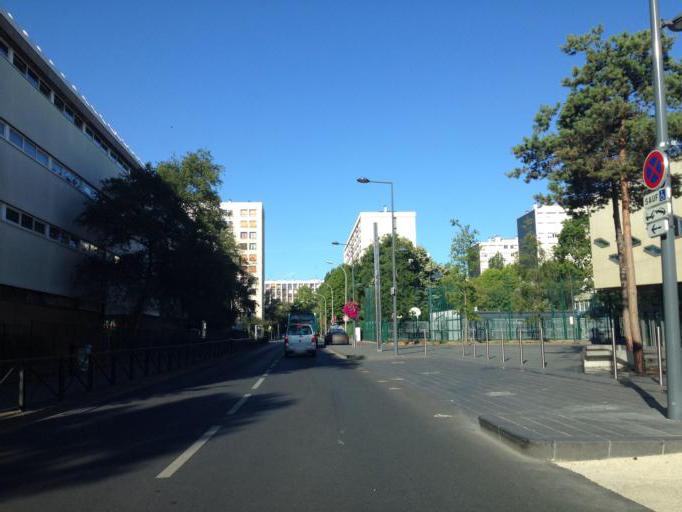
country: FR
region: Ile-de-France
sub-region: Departement des Hauts-de-Seine
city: Meudon
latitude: 48.7873
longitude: 2.2330
